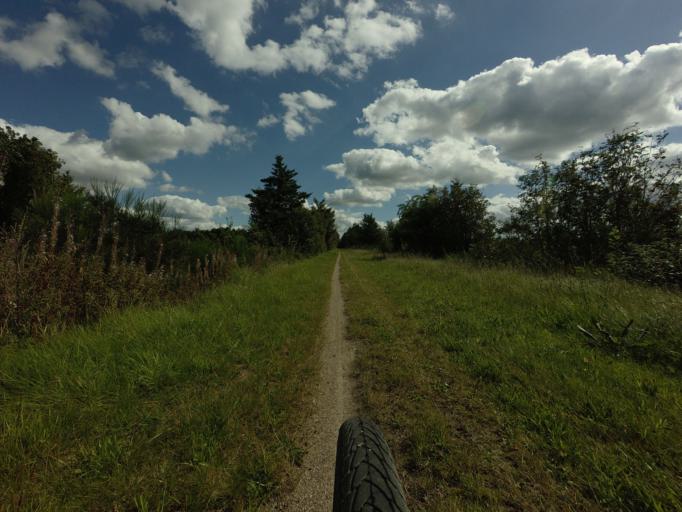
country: DK
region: Central Jutland
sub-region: Ikast-Brande Kommune
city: Brande
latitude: 55.9770
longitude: 9.1878
